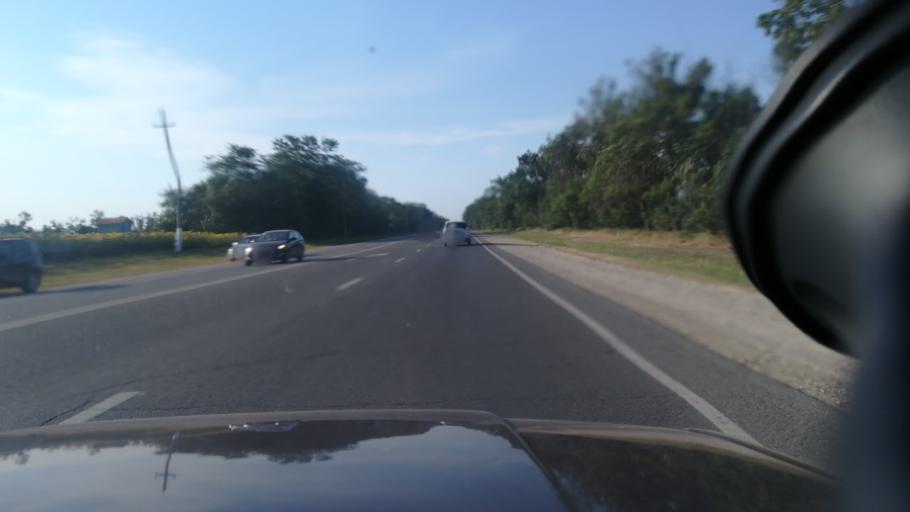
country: RU
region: Krasnodarskiy
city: Tsibanobalka
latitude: 45.0089
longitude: 37.3210
